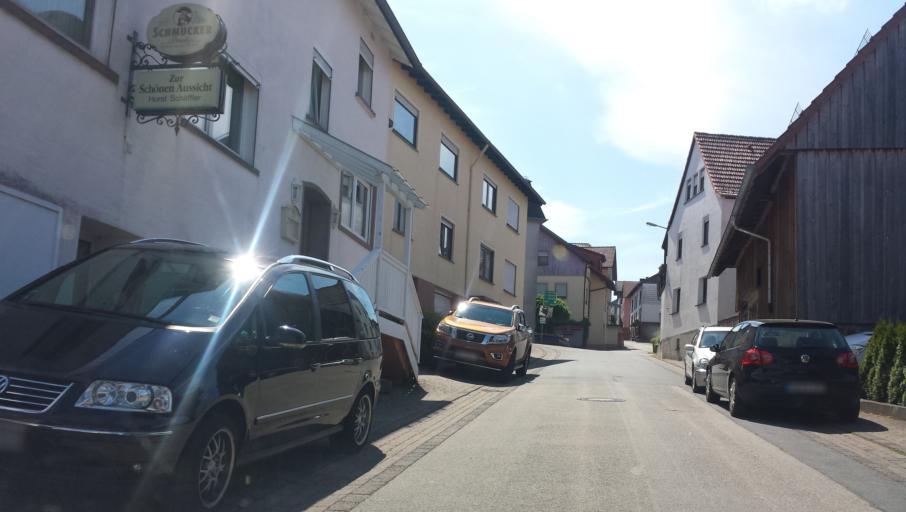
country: DE
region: Hesse
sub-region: Regierungsbezirk Darmstadt
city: Rothenberg
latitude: 49.4957
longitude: 8.9225
